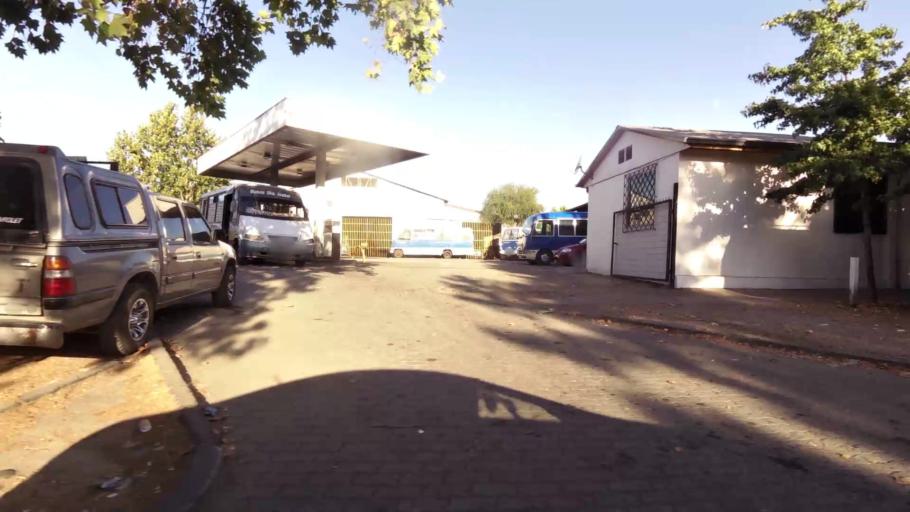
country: CL
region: Maule
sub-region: Provincia de Talca
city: Talca
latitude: -35.4329
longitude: -71.6483
